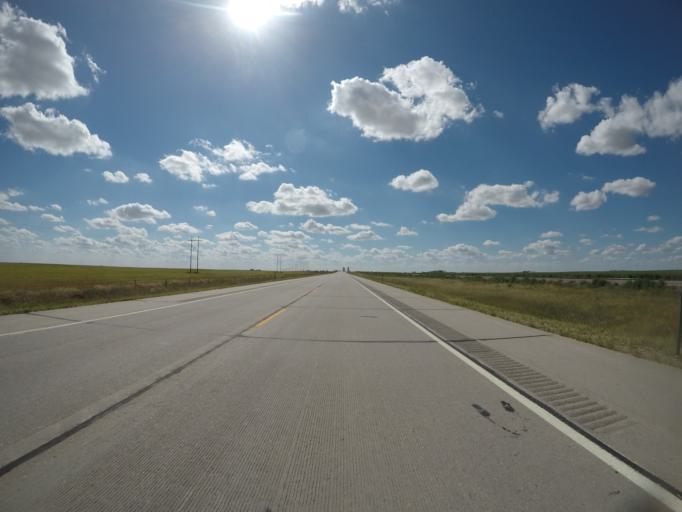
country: US
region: Colorado
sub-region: Phillips County
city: Holyoke
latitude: 40.6071
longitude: -102.4393
